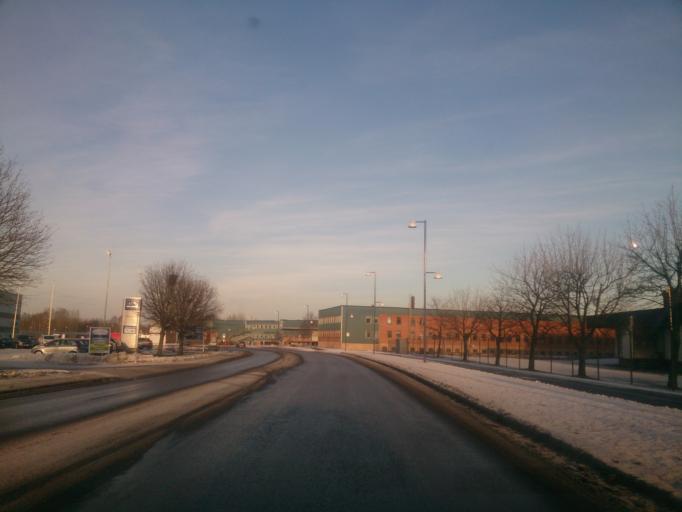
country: SE
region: OEstergoetland
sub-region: Norrkopings Kommun
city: Norrkoping
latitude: 58.6081
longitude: 16.1782
